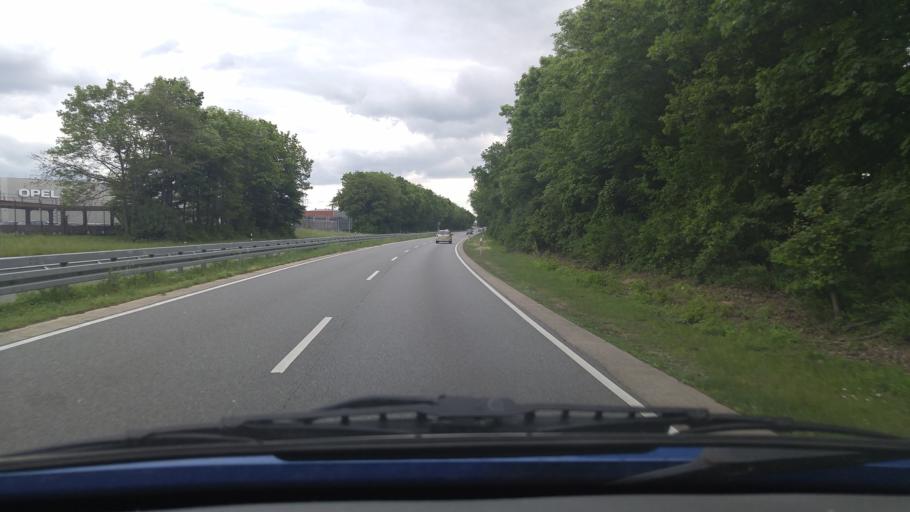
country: DE
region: Hesse
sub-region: Regierungsbezirk Darmstadt
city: Bischofsheim
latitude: 49.9909
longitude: 8.3747
